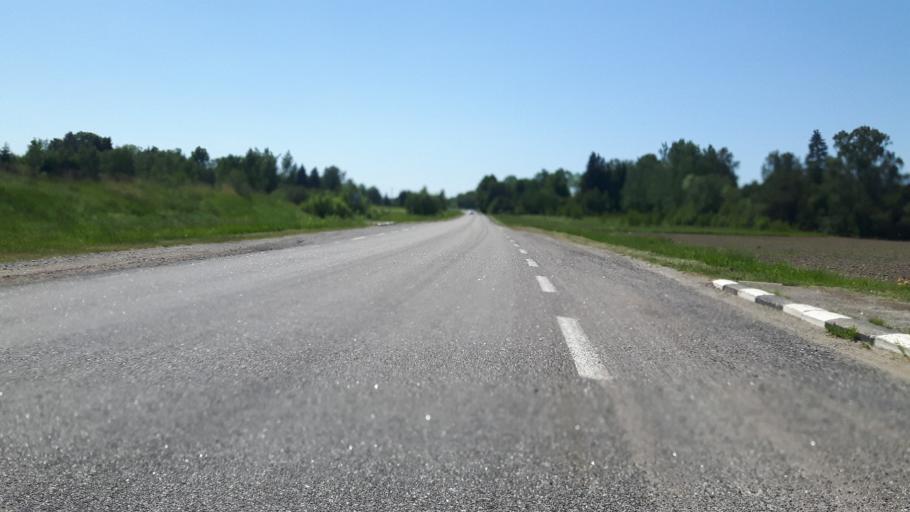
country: EE
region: Paernumaa
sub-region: Tootsi vald
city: Tootsi
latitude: 58.4952
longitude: 24.8451
